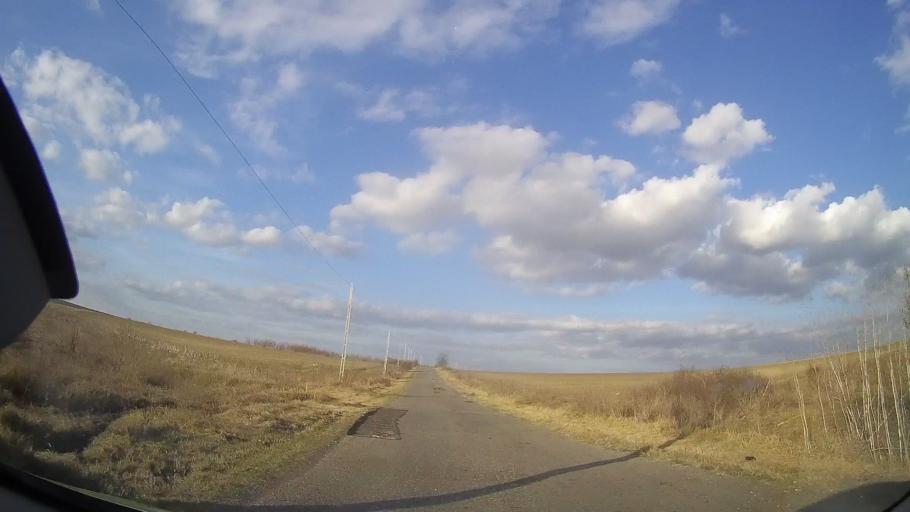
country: RO
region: Constanta
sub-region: Comuna Cerchezu
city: Cerchezu
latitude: 43.8435
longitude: 28.0984
